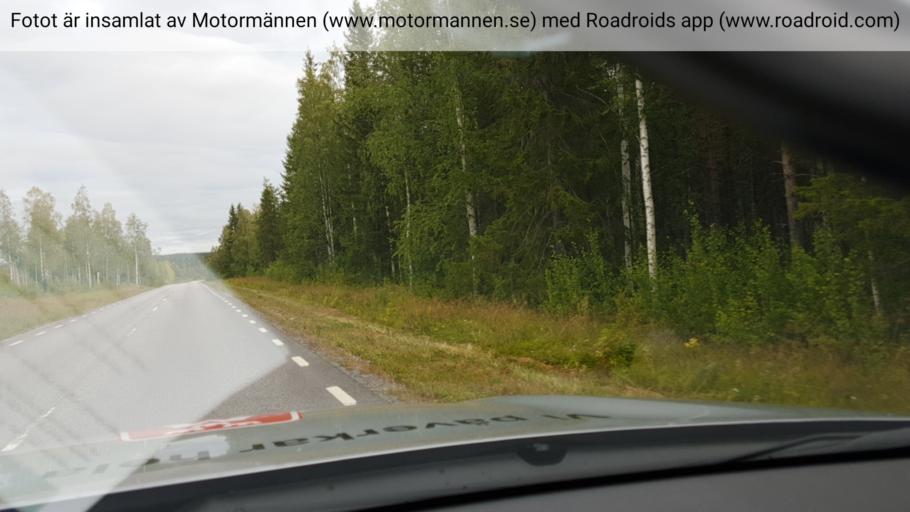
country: SE
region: Norrbotten
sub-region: Bodens Kommun
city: Boden
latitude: 65.7526
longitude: 21.5974
